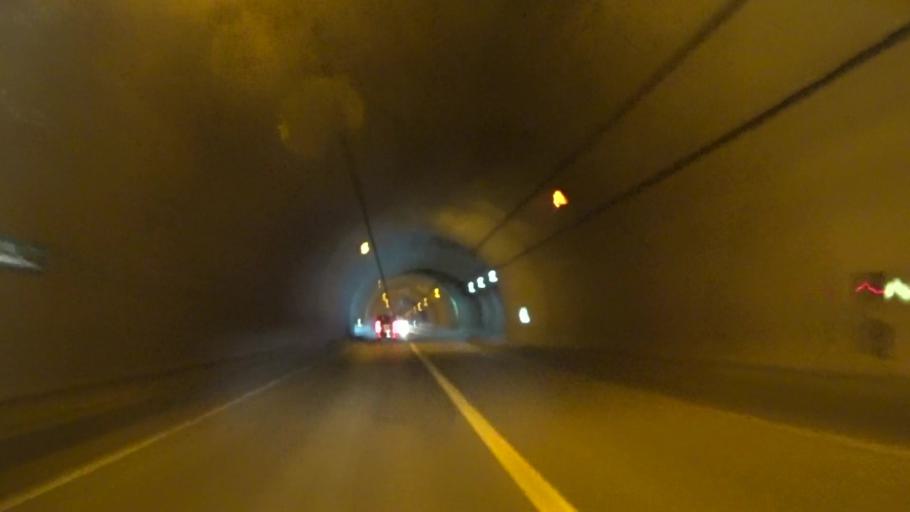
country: JP
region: Kyoto
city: Fukuchiyama
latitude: 35.4101
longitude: 135.0383
